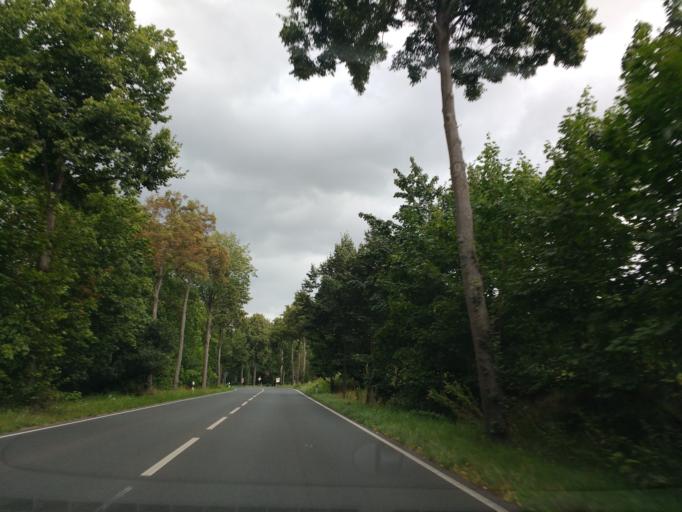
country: DE
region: Lower Saxony
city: Glandorf
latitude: 52.0804
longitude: 8.0042
